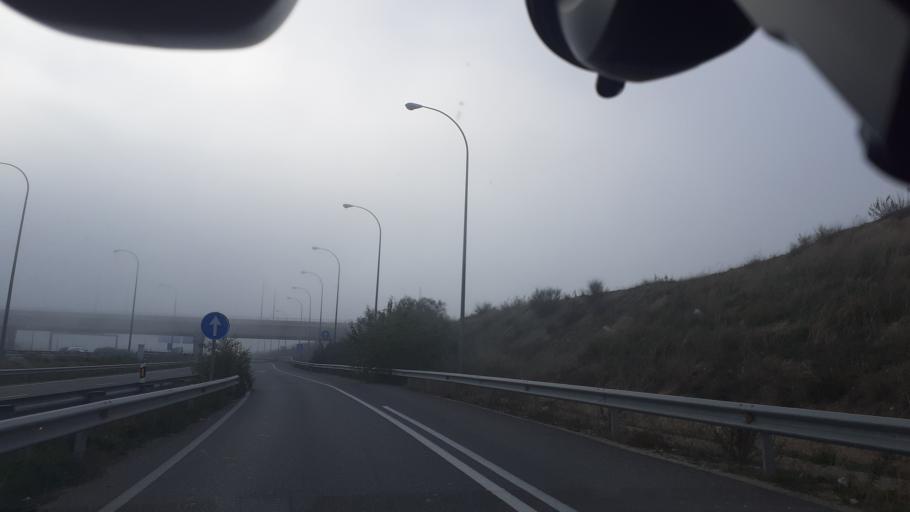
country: ES
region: Madrid
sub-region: Provincia de Madrid
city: Coslada
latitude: 40.4110
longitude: -3.5586
